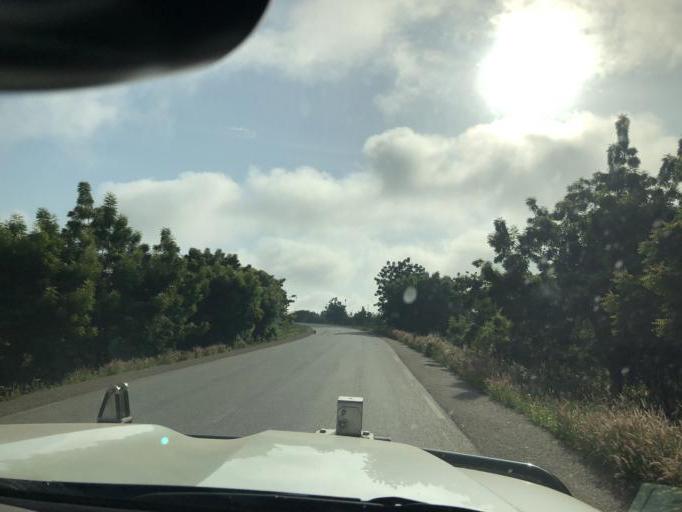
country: CM
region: North Province
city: Pitoa
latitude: 9.4937
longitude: 13.6861
